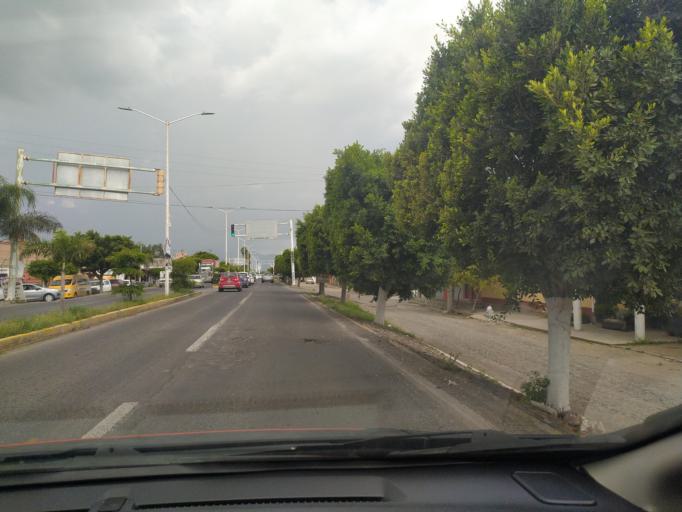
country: MX
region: Jalisco
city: Villa Corona
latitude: 20.4137
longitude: -103.6656
